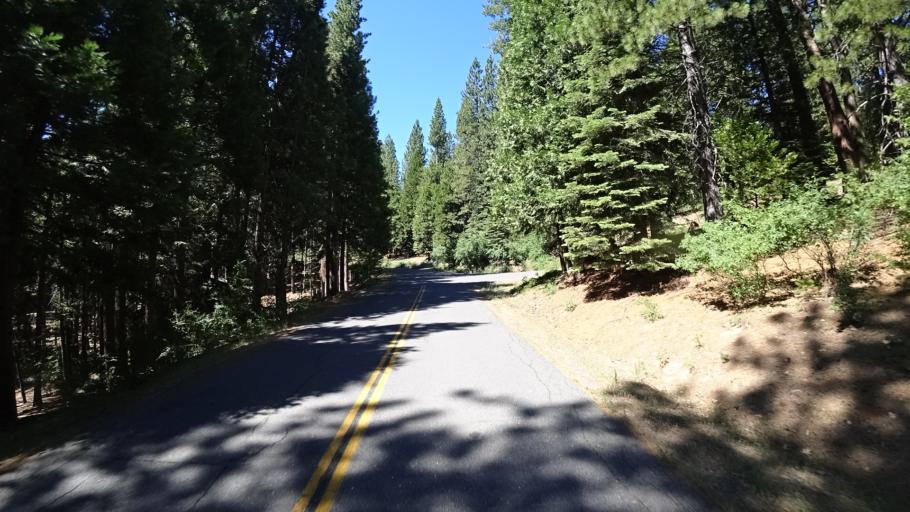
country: US
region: California
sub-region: Calaveras County
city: Arnold
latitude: 38.2870
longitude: -120.2830
